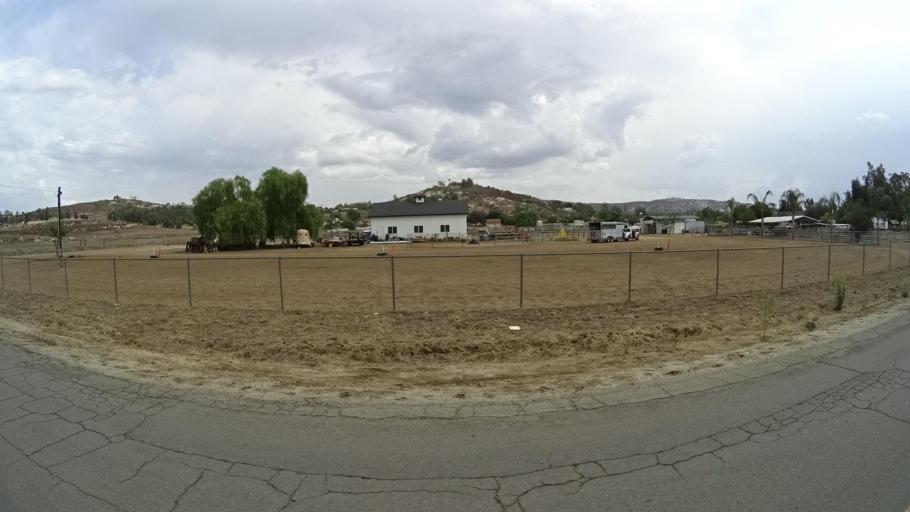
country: US
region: California
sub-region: San Diego County
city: Ramona
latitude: 33.0725
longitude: -116.8589
